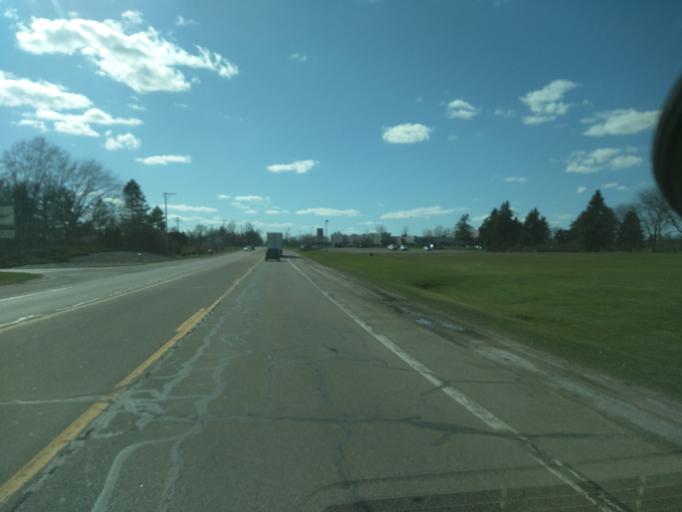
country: US
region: Michigan
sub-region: Ingham County
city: Edgemont Park
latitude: 42.7738
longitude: -84.6126
